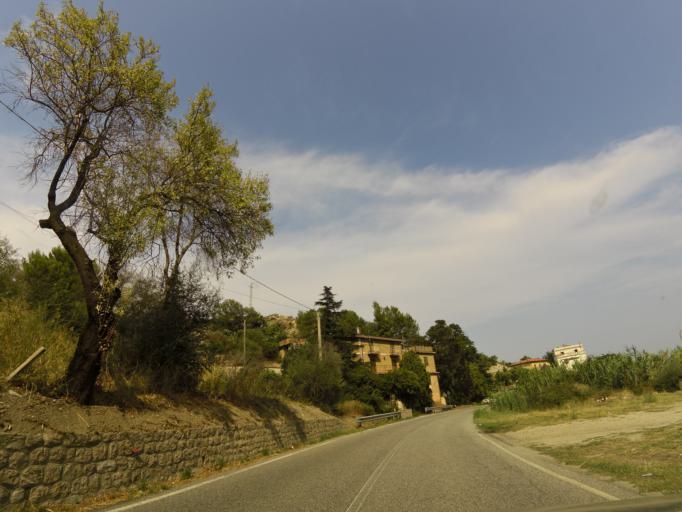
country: IT
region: Calabria
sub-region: Provincia di Reggio Calabria
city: Stilo
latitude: 38.4669
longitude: 16.5033
